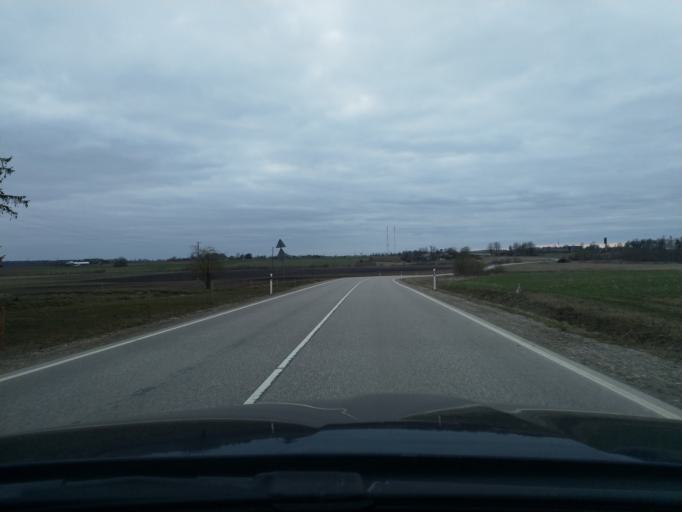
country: LV
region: Talsu Rajons
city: Sabile
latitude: 56.9429
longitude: 22.4189
